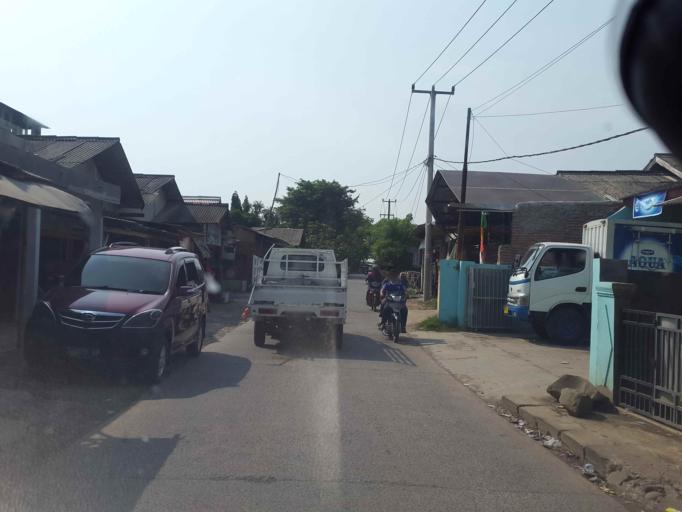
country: ID
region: West Java
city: Cikarang
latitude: -6.2122
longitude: 107.1453
